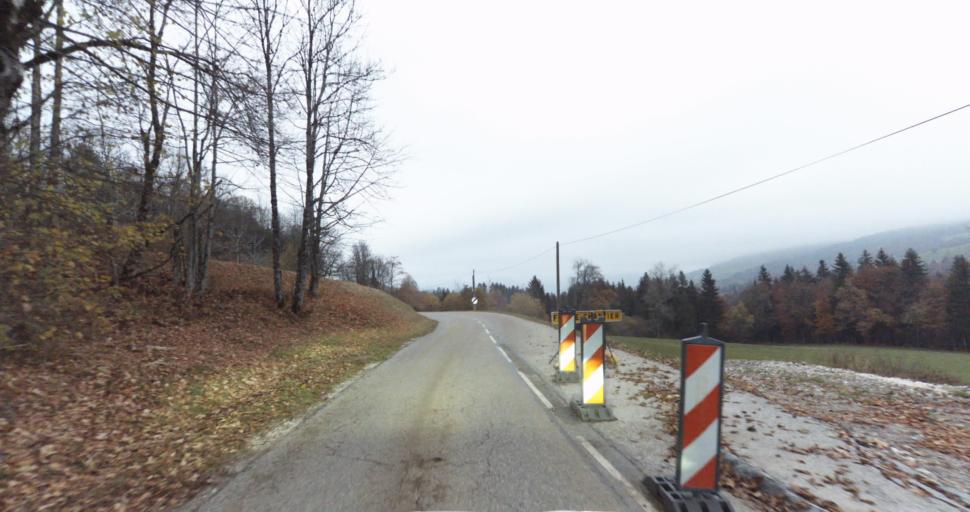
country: FR
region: Rhone-Alpes
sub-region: Departement de la Haute-Savoie
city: Saint-Jorioz
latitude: 45.7833
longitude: 6.1323
